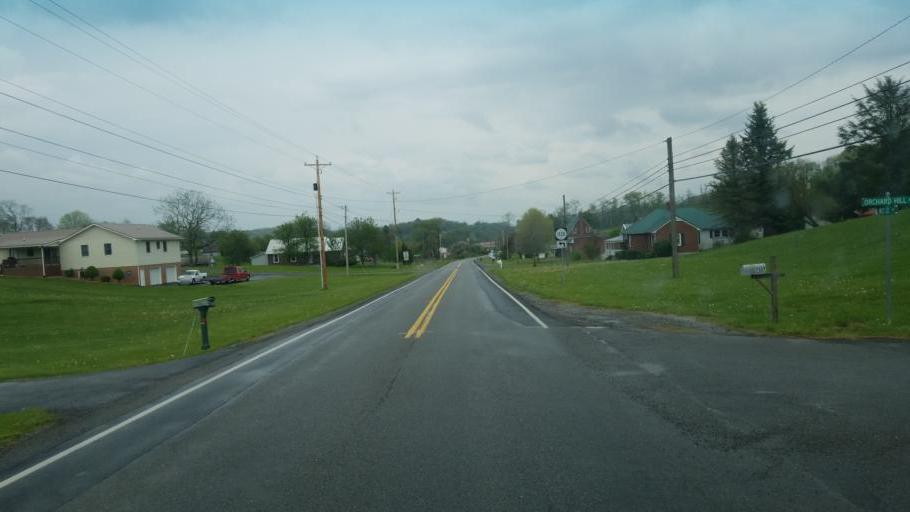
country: US
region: Virginia
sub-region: Wythe County
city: Rural Retreat
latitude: 36.9086
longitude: -81.2827
